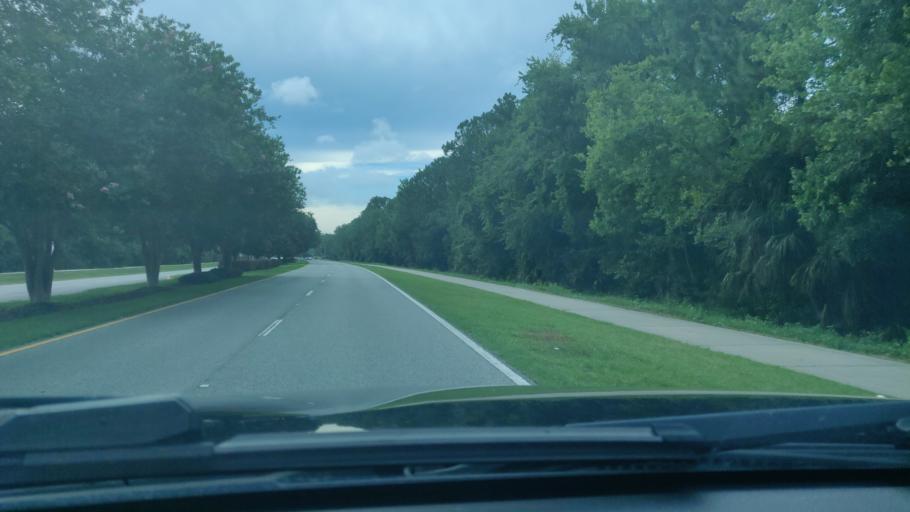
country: US
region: Florida
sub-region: Flagler County
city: Palm Coast
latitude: 29.5430
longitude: -81.2298
